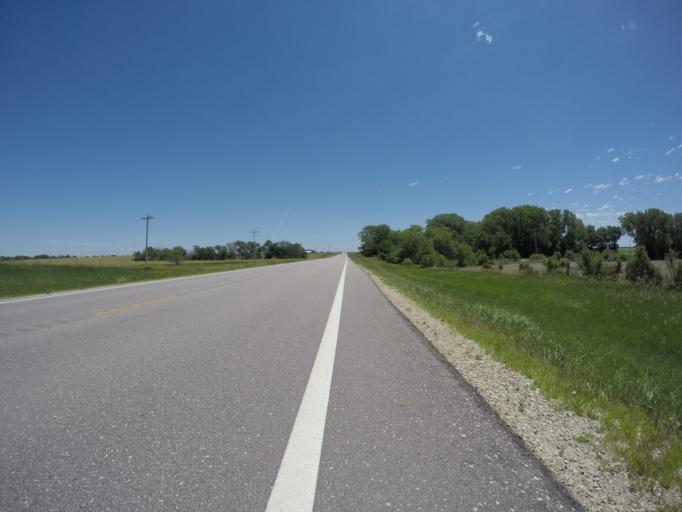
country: US
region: Kansas
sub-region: Republic County
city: Belleville
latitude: 39.8127
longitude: -97.6910
